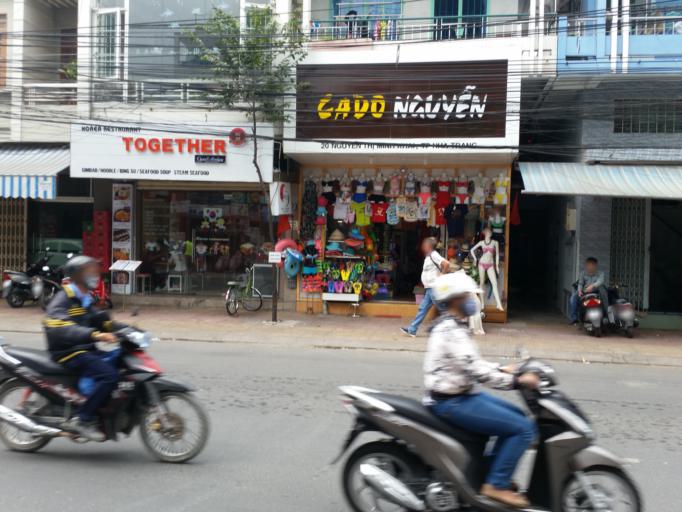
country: VN
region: Khanh Hoa
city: Nha Trang
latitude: 12.2386
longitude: 109.1948
